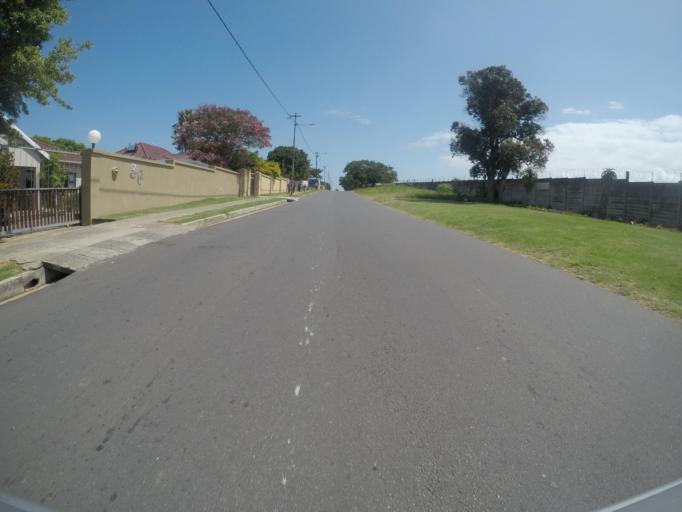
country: ZA
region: Eastern Cape
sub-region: Buffalo City Metropolitan Municipality
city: East London
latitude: -32.9745
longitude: 27.8705
